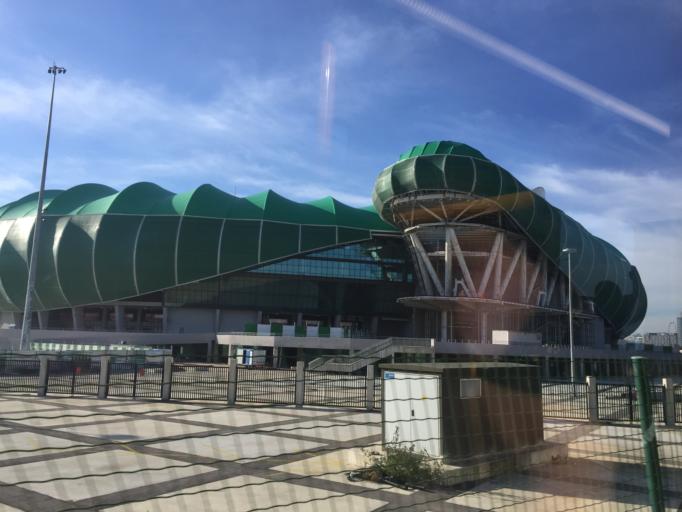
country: TR
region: Bursa
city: Yildirim
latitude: 40.2129
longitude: 29.0103
